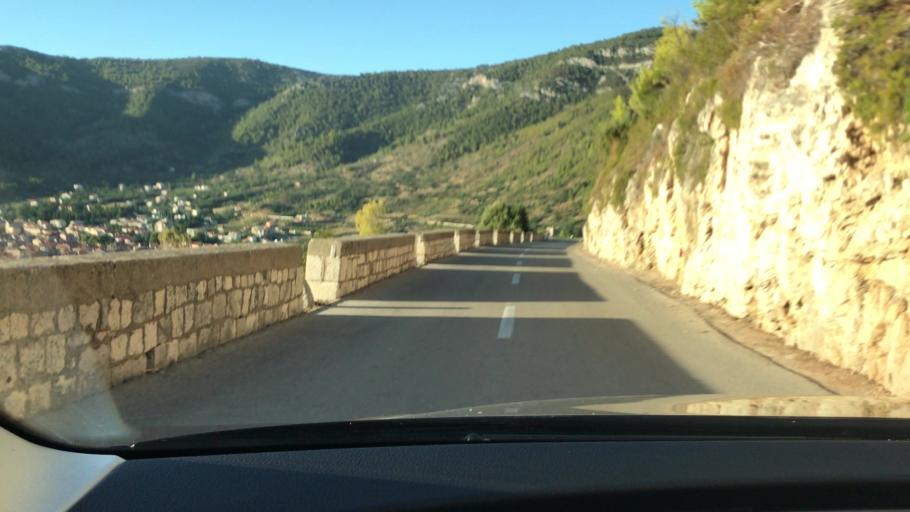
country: HR
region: Splitsko-Dalmatinska
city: Komiza
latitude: 43.0358
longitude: 16.0948
